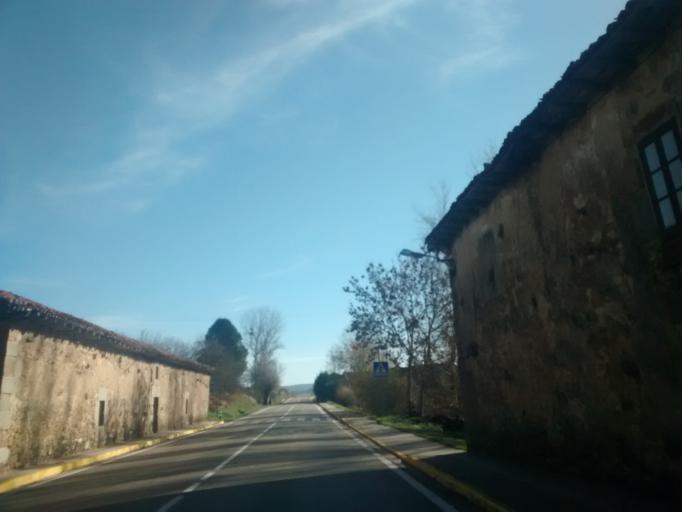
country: ES
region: Castille and Leon
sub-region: Provincia de Burgos
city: Arija
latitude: 42.9821
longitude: -3.8127
